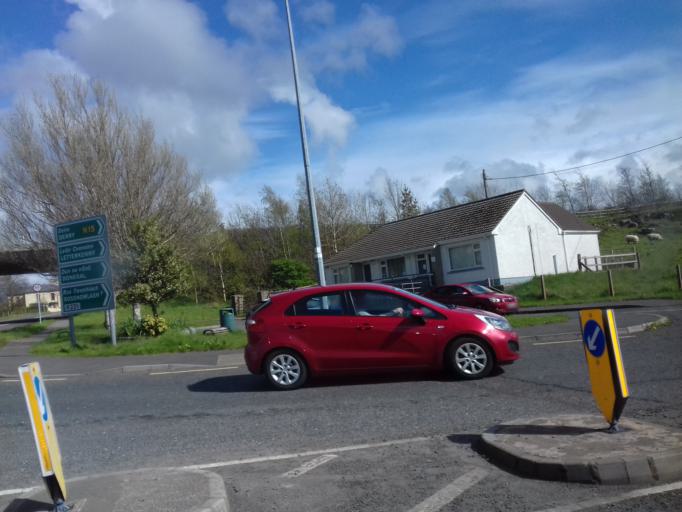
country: IE
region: Ulster
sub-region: County Donegal
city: Ballyshannon
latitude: 54.4996
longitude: -8.1838
